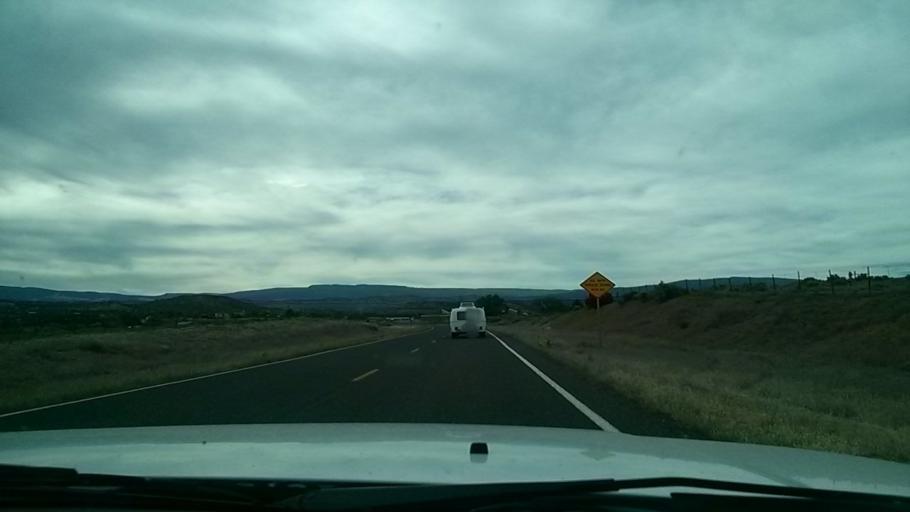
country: US
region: Utah
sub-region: Wayne County
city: Loa
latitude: 37.7620
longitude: -111.5797
